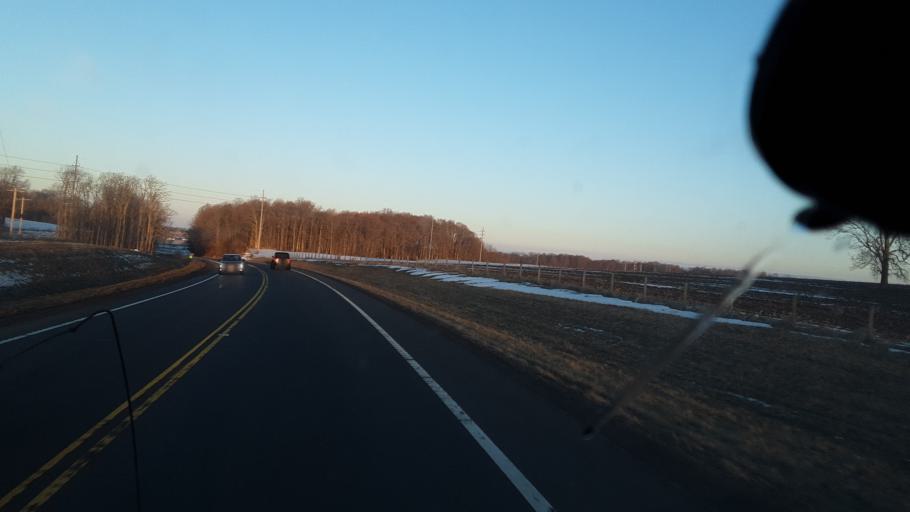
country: US
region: Ohio
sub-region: Perry County
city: Somerset
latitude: 39.8292
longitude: -82.3299
